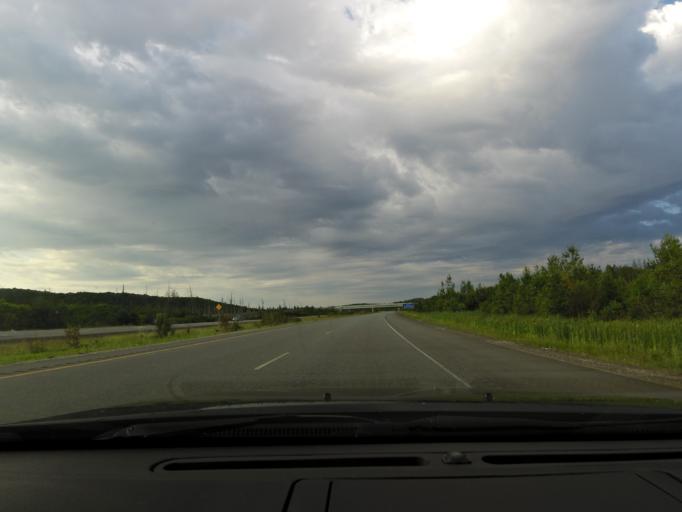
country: CA
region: Ontario
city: Huntsville
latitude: 45.4491
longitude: -79.2458
